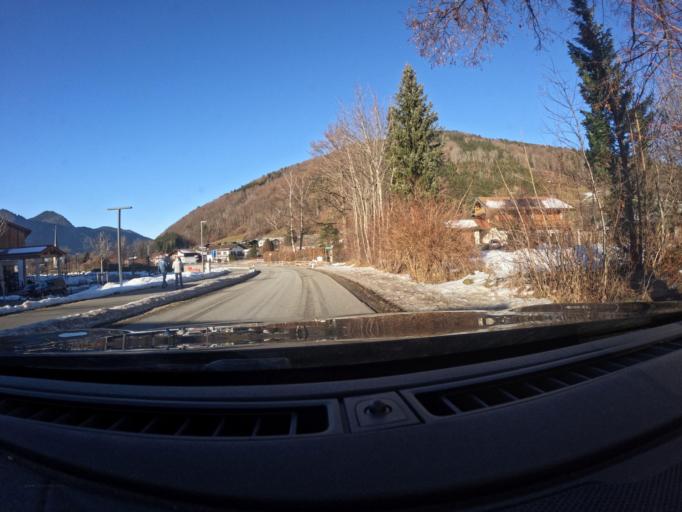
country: DE
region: Bavaria
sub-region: Upper Bavaria
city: Ruhpolding
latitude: 47.7549
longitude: 12.6667
